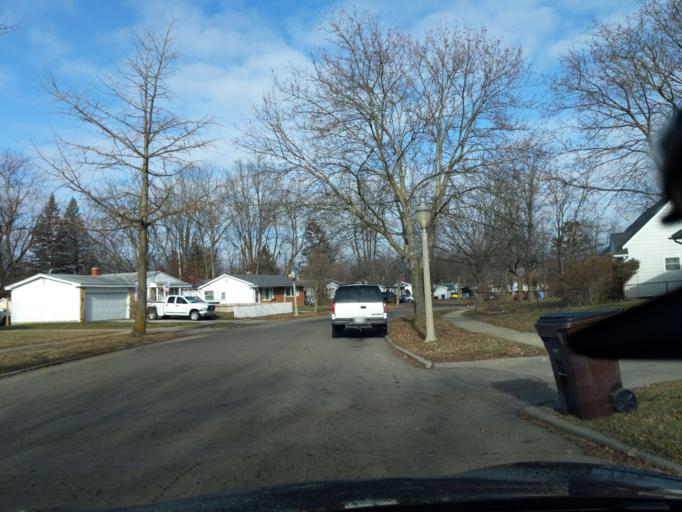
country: US
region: Michigan
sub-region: Eaton County
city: Waverly
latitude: 42.6950
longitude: -84.5984
